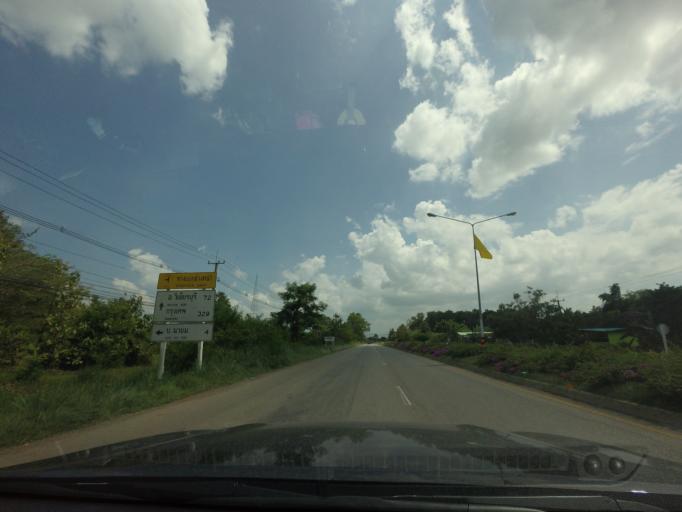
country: TH
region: Phetchabun
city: Phetchabun
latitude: 16.2524
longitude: 101.0651
